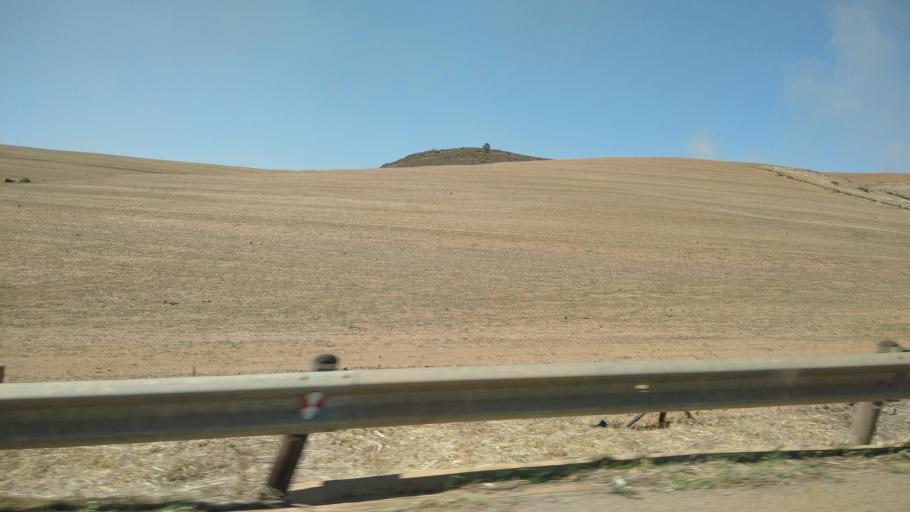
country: ZA
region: Western Cape
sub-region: West Coast District Municipality
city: Malmesbury
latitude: -33.3767
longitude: 18.6639
